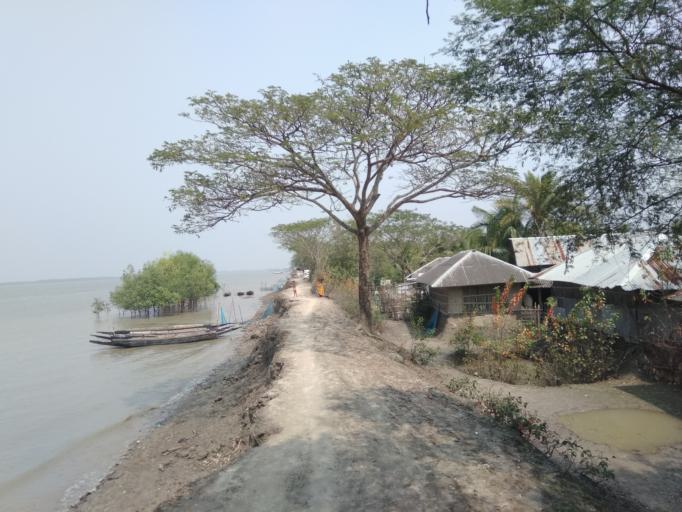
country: IN
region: West Bengal
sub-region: North 24 Parganas
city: Gosaba
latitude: 22.2485
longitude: 89.2499
